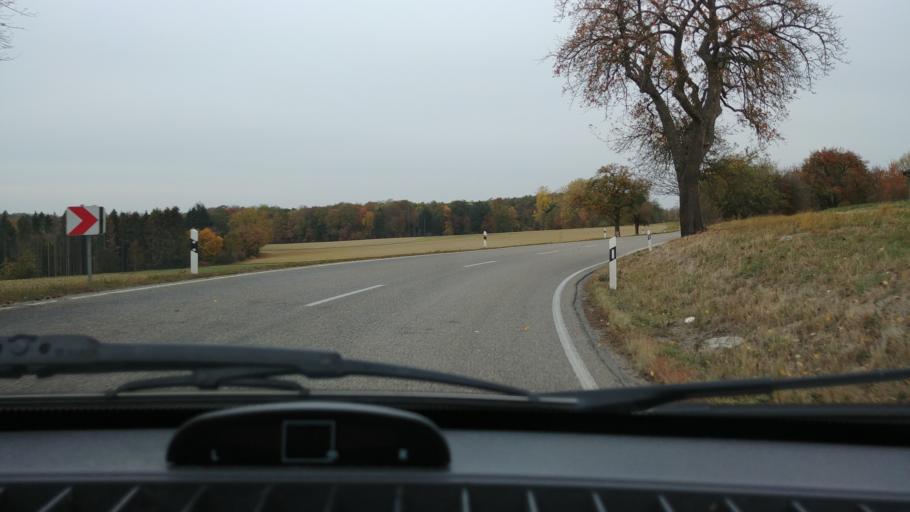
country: DE
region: Baden-Wuerttemberg
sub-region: Regierungsbezirk Stuttgart
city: Wallhausen
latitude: 49.2152
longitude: 10.0615
